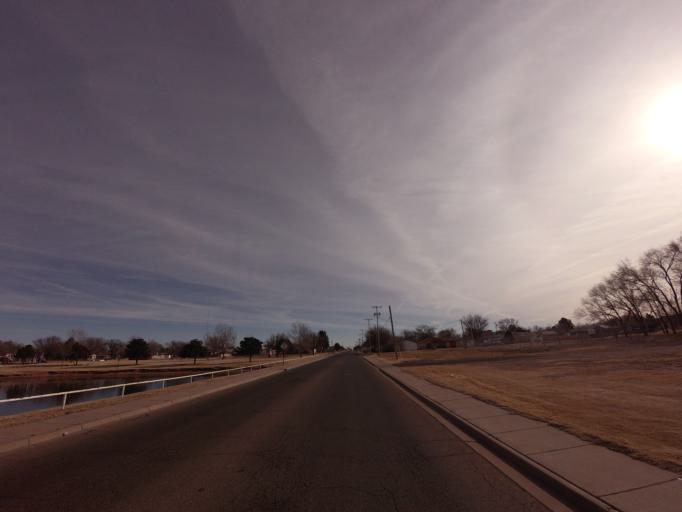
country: US
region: New Mexico
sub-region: Curry County
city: Clovis
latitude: 34.4120
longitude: -103.2189
